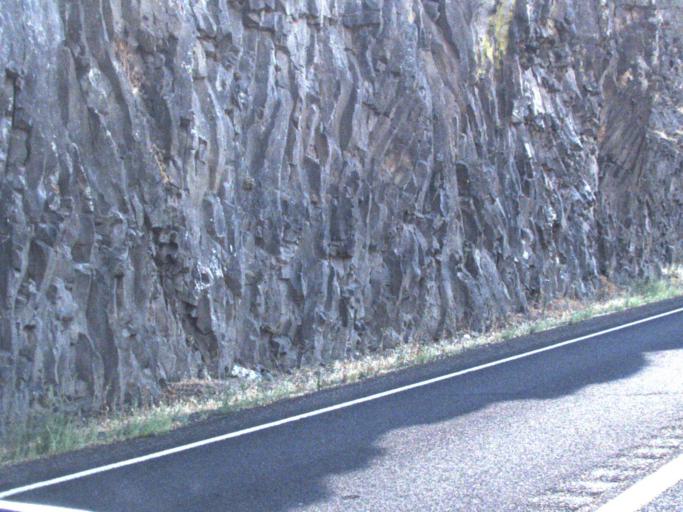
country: US
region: Washington
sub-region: Yakima County
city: Selah
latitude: 46.7051
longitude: -120.4720
